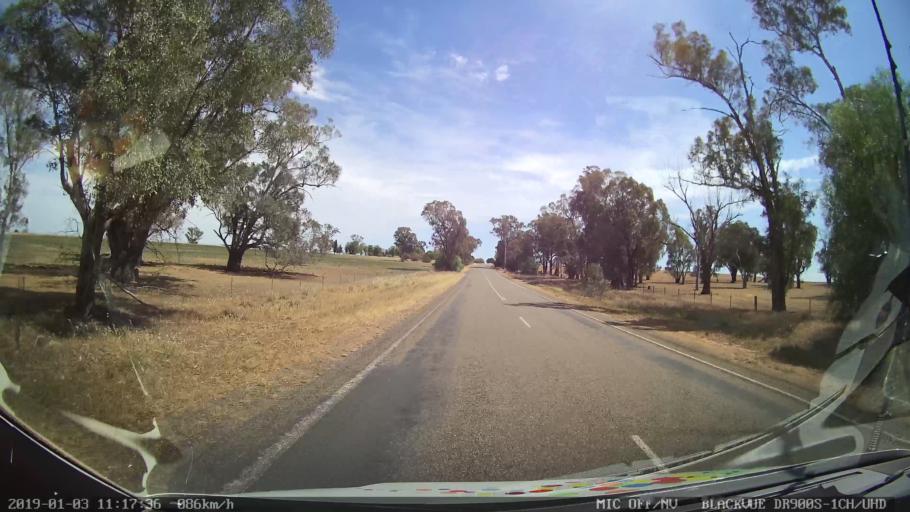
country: AU
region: New South Wales
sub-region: Young
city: Young
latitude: -34.1366
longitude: 148.2652
